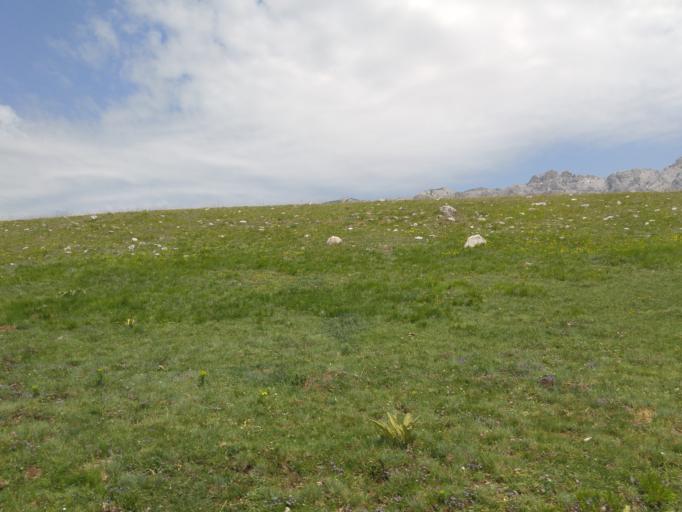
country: IT
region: Abruzzo
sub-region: Provincia dell' Aquila
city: Santo Stefano di Sessanio
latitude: 42.3999
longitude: 13.6537
